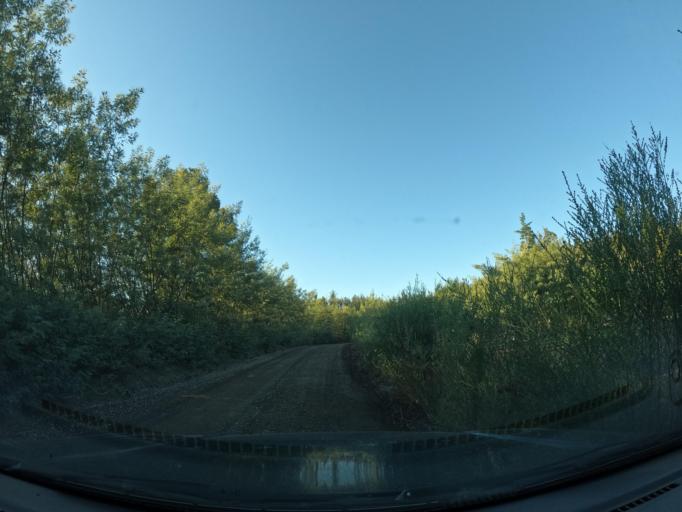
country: CL
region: Biobio
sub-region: Provincia de Concepcion
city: Chiguayante
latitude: -37.0287
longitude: -72.8730
